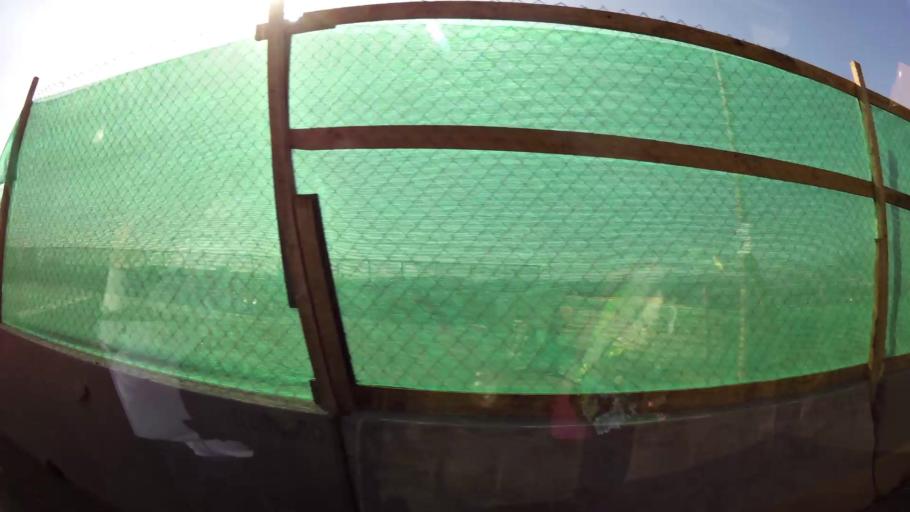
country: CL
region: Santiago Metropolitan
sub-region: Provincia de Chacabuco
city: Chicureo Abajo
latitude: -33.3341
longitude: -70.7146
